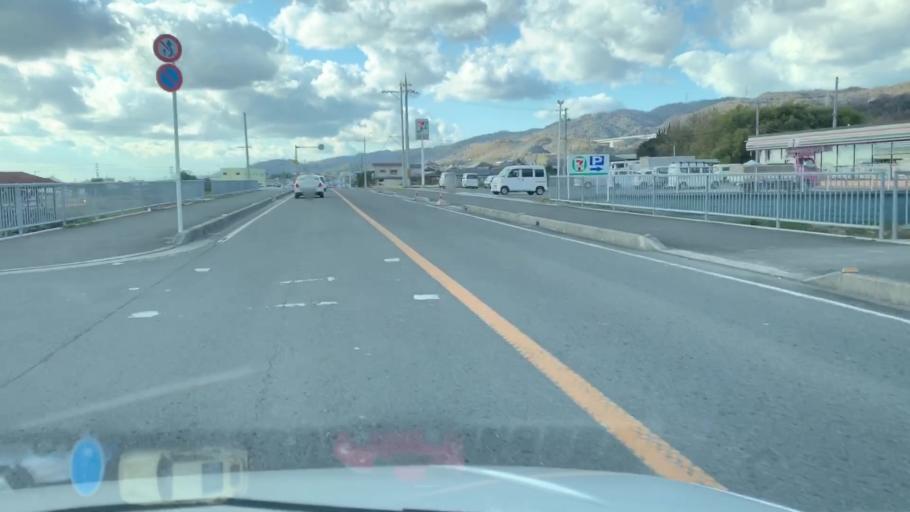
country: JP
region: Wakayama
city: Iwade
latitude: 34.2710
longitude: 135.2746
